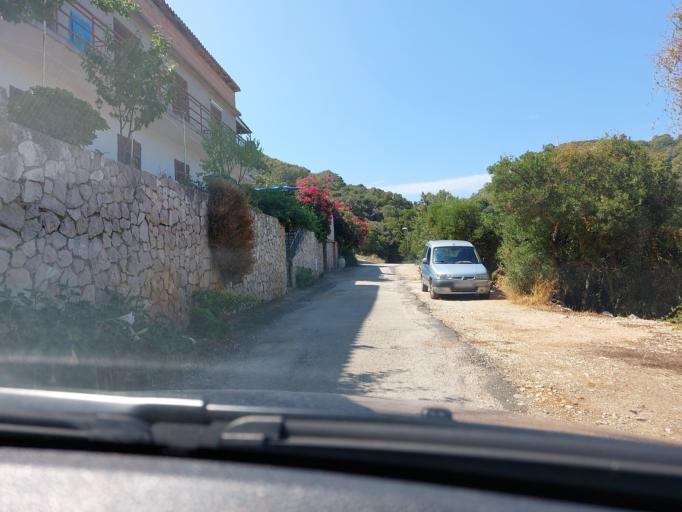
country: HR
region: Dubrovacko-Neretvanska
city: Smokvica
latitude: 42.7671
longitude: 16.8261
